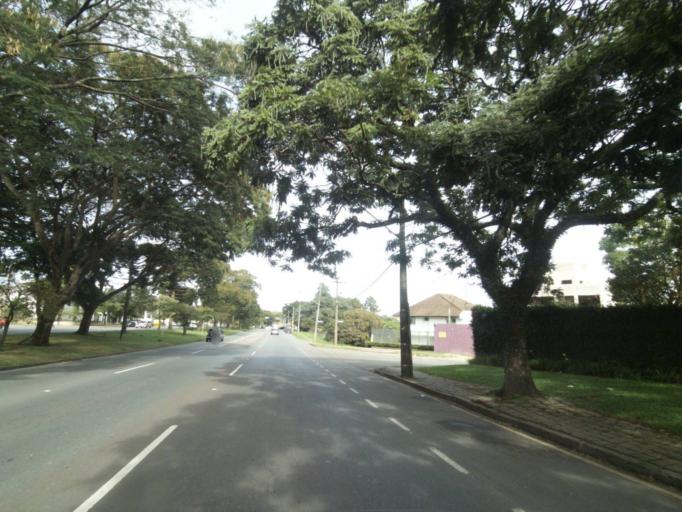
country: BR
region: Parana
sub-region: Curitiba
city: Curitiba
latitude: -25.4214
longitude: -49.2404
